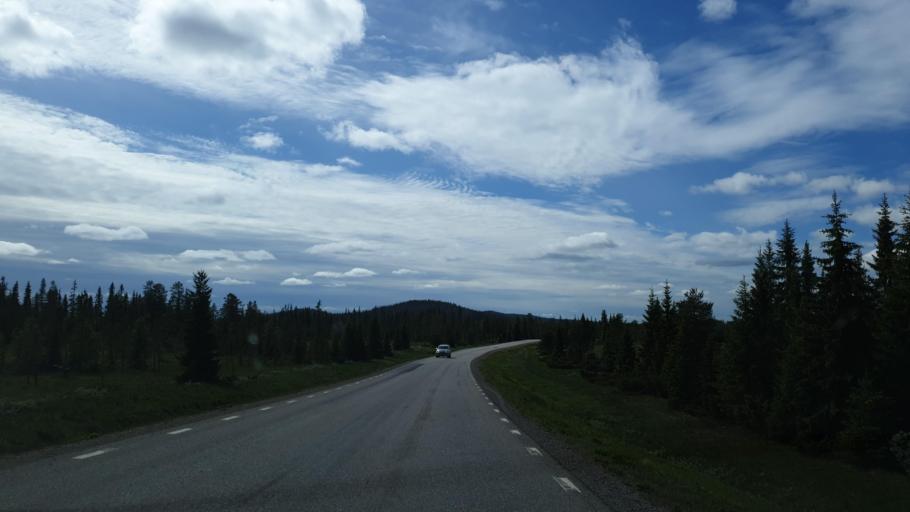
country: SE
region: Vaesterbotten
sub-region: Mala Kommun
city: Mala
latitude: 65.5740
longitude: 18.4312
